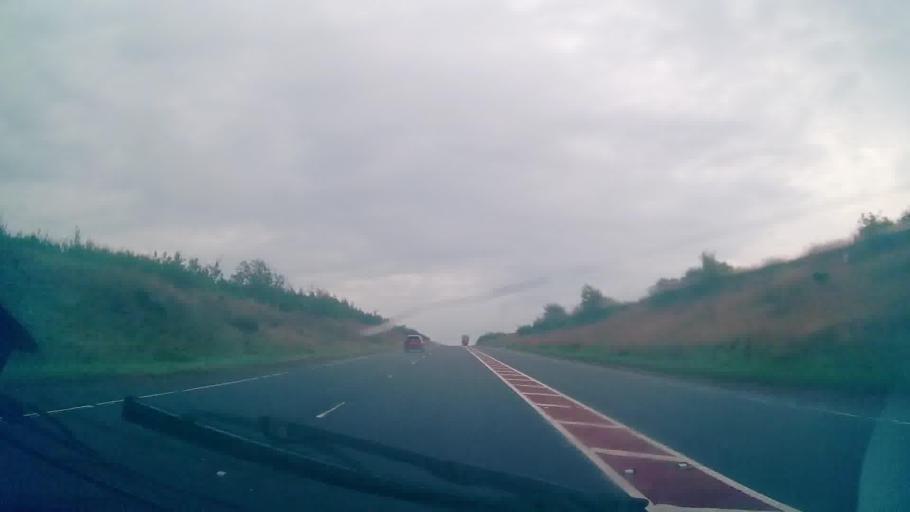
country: GB
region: Scotland
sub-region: Dumfries and Galloway
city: Lockerbie
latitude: 55.0250
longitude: -3.3807
